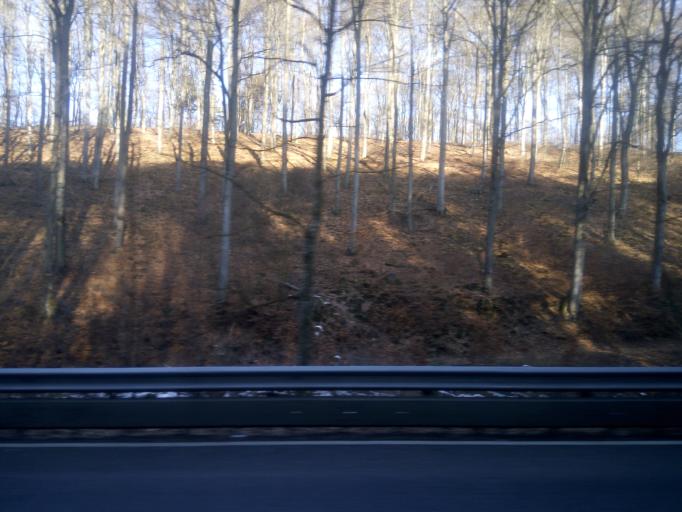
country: LU
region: Luxembourg
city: Helmsange
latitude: 49.6461
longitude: 6.1682
